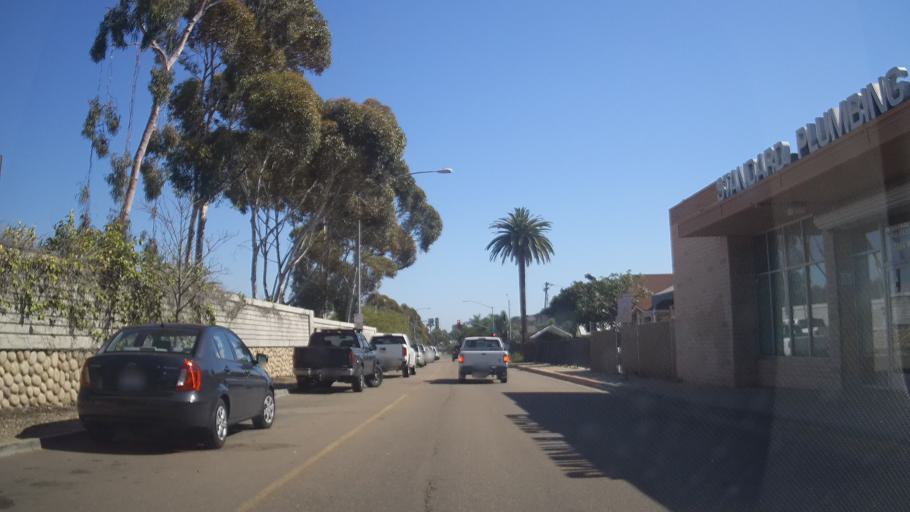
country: US
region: California
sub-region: San Diego County
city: San Diego
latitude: 32.7492
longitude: -117.1095
